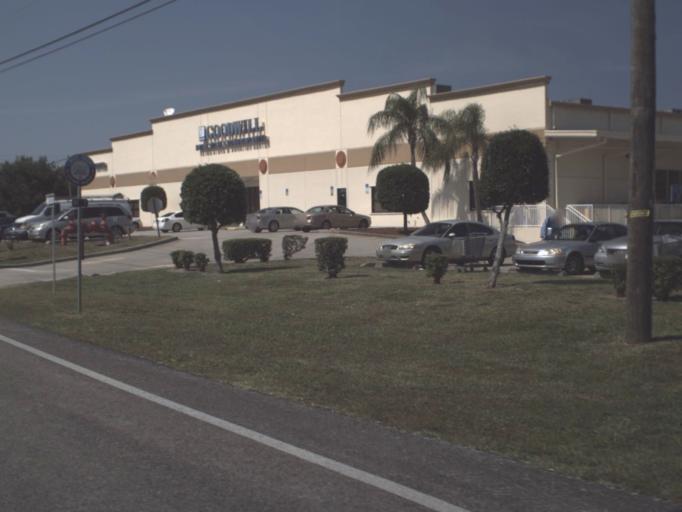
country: US
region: Florida
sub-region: Brevard County
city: Rockledge
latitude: 28.2735
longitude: -80.6924
